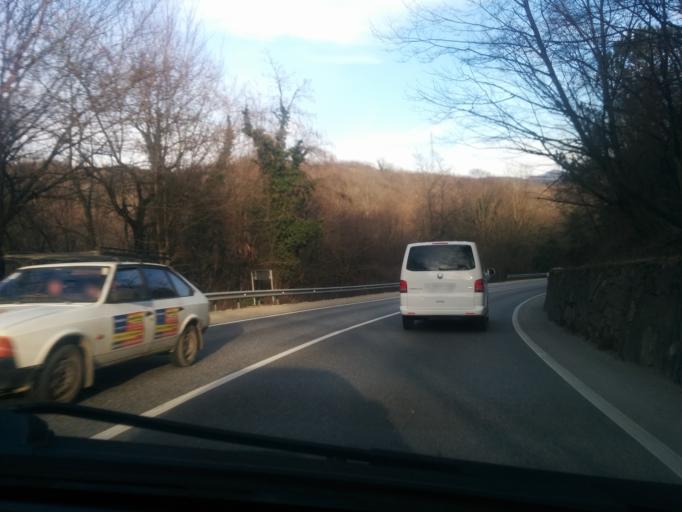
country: RU
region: Krasnodarskiy
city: Ol'ginka
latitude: 44.2402
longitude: 38.8928
